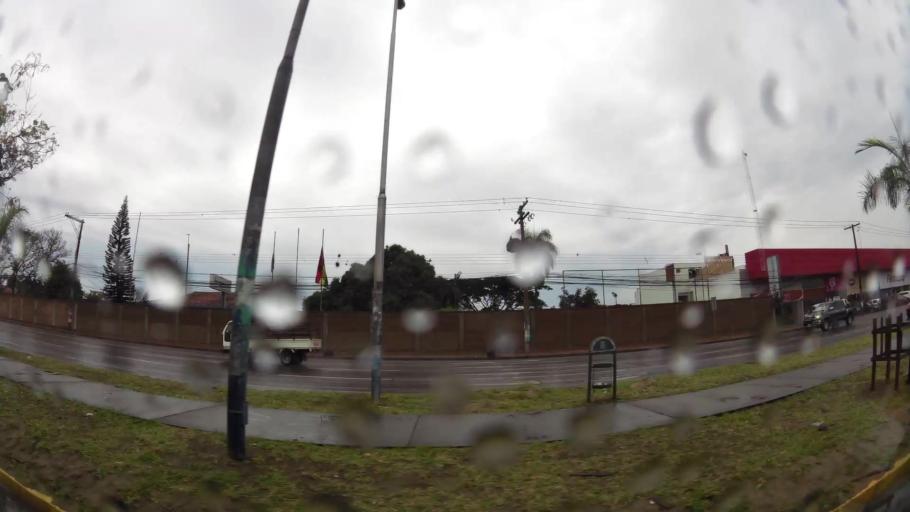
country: BO
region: Santa Cruz
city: Santa Cruz de la Sierra
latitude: -17.8083
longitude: -63.2042
